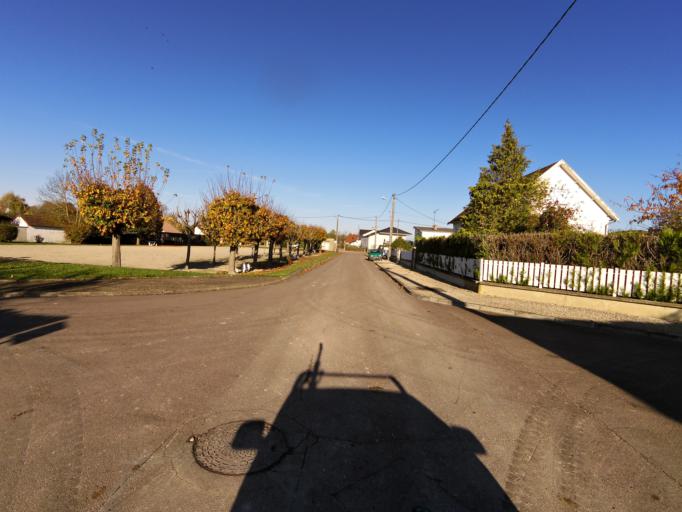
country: FR
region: Champagne-Ardenne
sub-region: Departement de l'Aube
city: Rosieres-pres-Troyes
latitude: 48.2540
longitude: 4.0558
